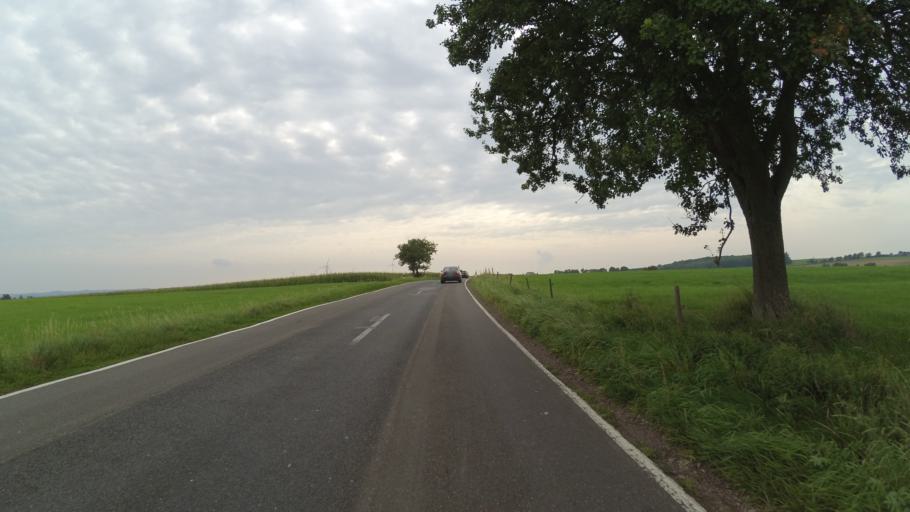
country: DE
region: Rheinland-Pfalz
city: Merzkirchen
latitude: 49.5852
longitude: 6.4838
